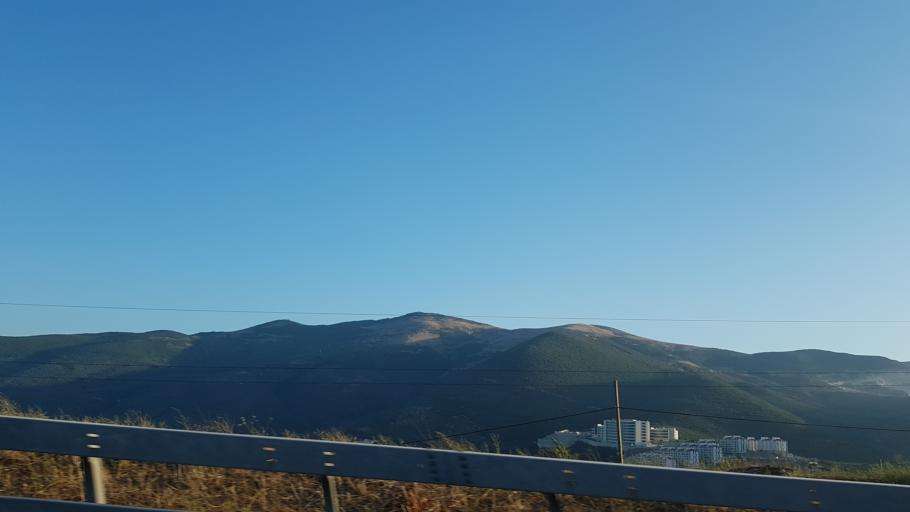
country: TR
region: Bursa
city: Umurbey
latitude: 40.4221
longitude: 29.1848
